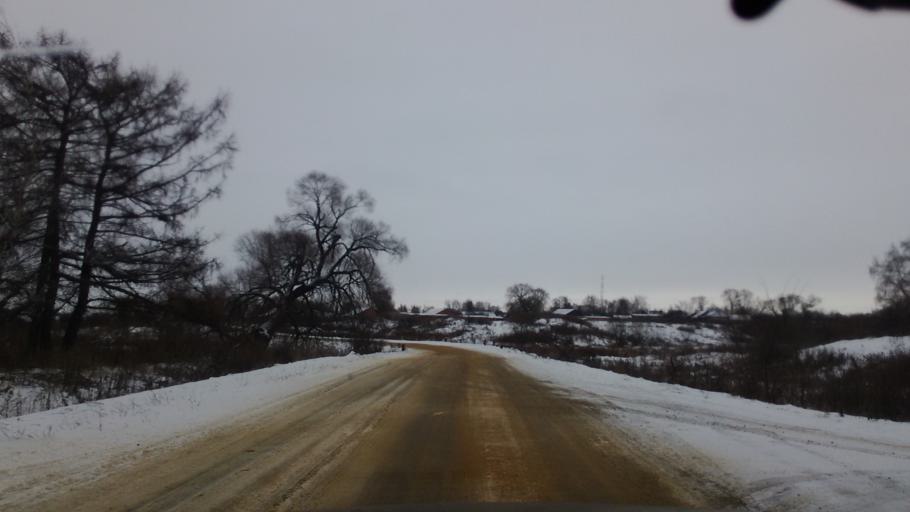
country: RU
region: Tula
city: Bogoroditsk
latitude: 53.7647
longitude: 37.9811
